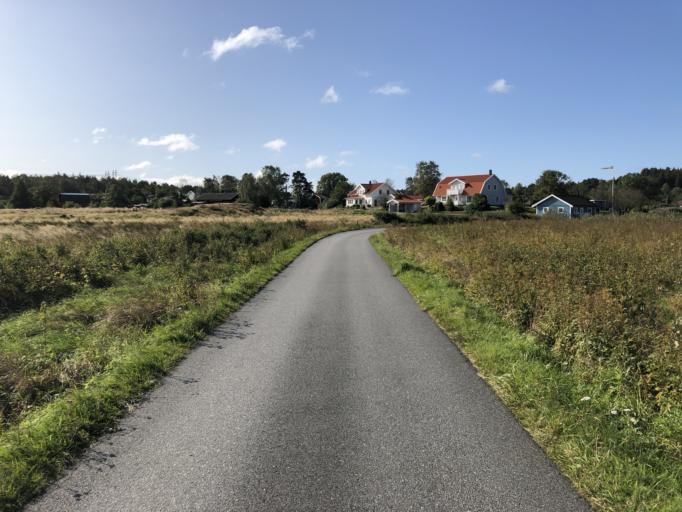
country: SE
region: Vaestra Goetaland
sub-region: Goteborg
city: Torslanda
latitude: 57.7366
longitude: 11.8177
